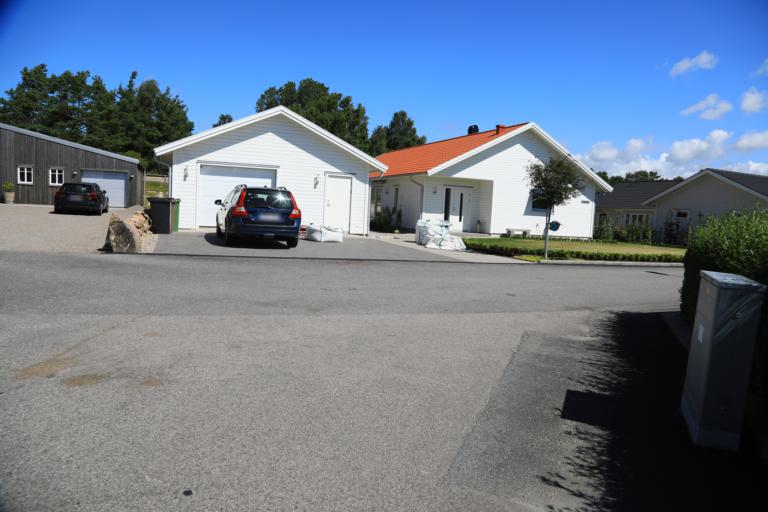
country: SE
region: Halland
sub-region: Varbergs Kommun
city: Traslovslage
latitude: 57.0997
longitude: 12.2958
